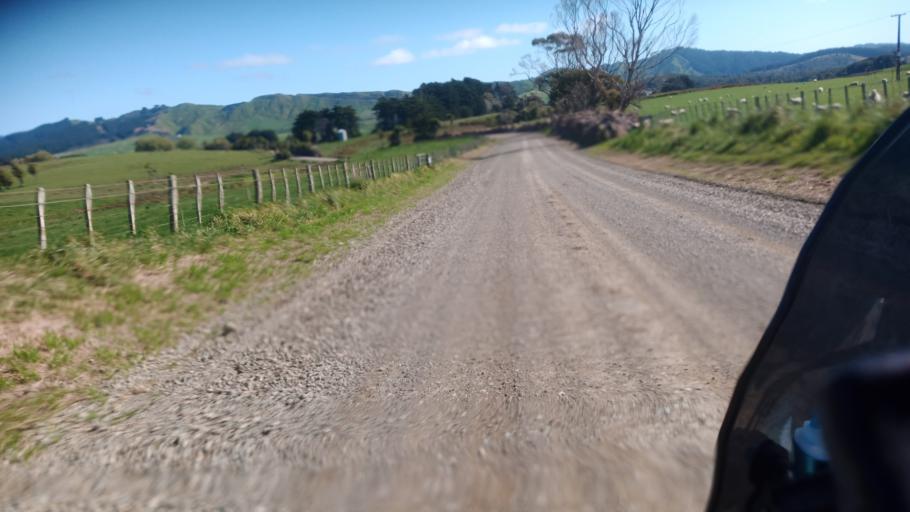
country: NZ
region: Gisborne
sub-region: Gisborne District
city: Gisborne
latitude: -39.1378
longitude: 177.9328
